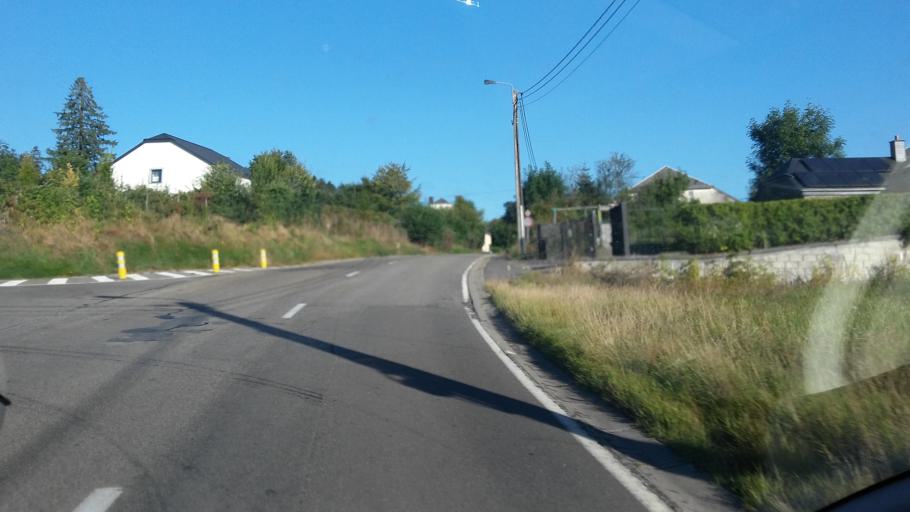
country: BE
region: Wallonia
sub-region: Province du Luxembourg
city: Neufchateau
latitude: 49.8316
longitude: 5.4796
